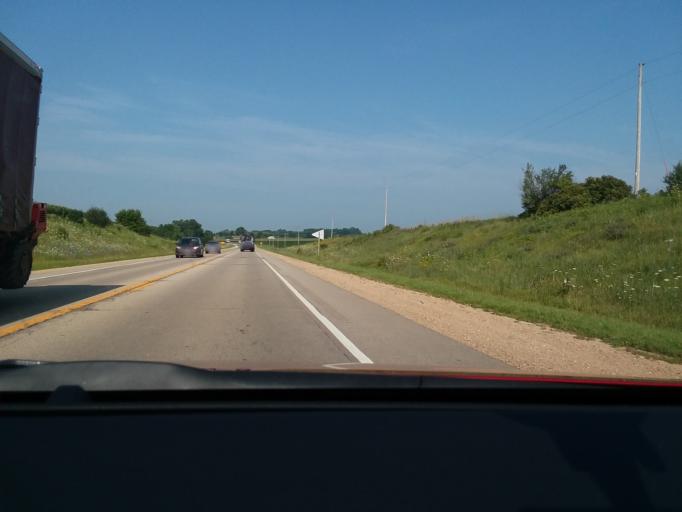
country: US
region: Wisconsin
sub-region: Dane County
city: Windsor
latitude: 43.1957
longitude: -89.3740
